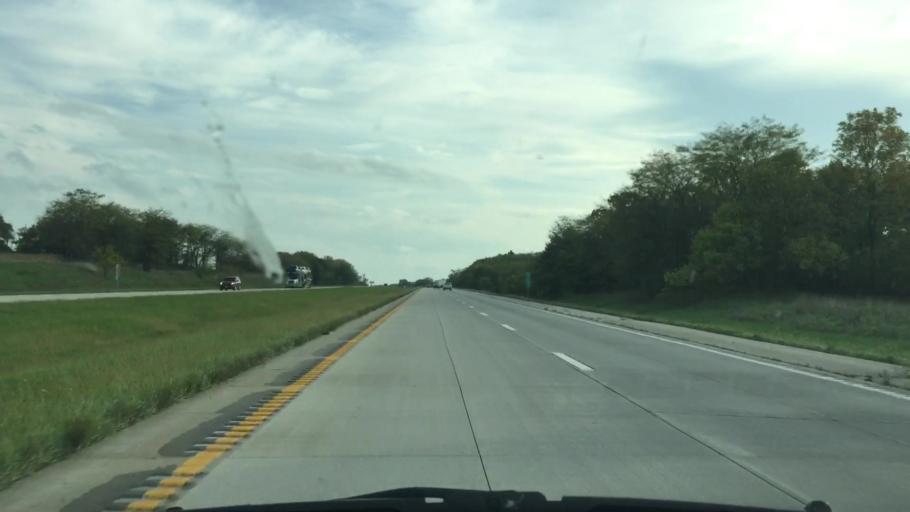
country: US
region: Missouri
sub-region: Daviess County
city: Gallatin
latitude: 40.0130
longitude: -94.0965
